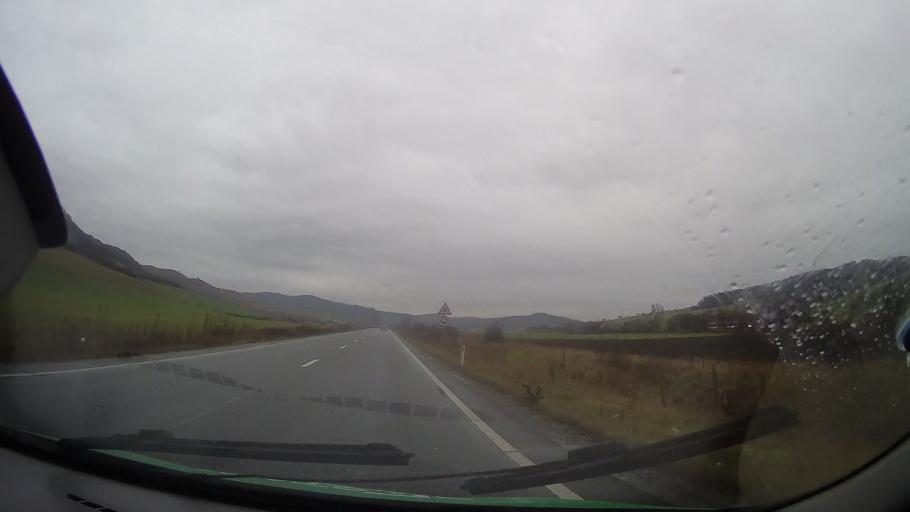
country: RO
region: Bistrita-Nasaud
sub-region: Comuna Teaca
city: Teaca
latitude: 46.9317
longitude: 24.4810
